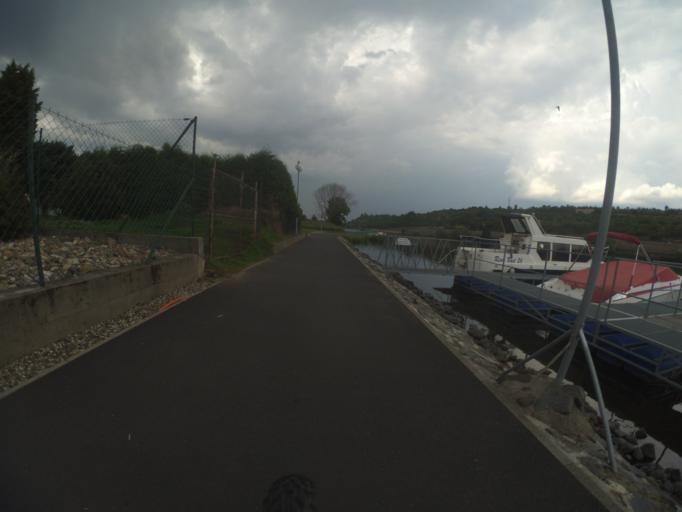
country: CZ
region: Central Bohemia
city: Dolni Berkovice
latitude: 50.3952
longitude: 14.4553
